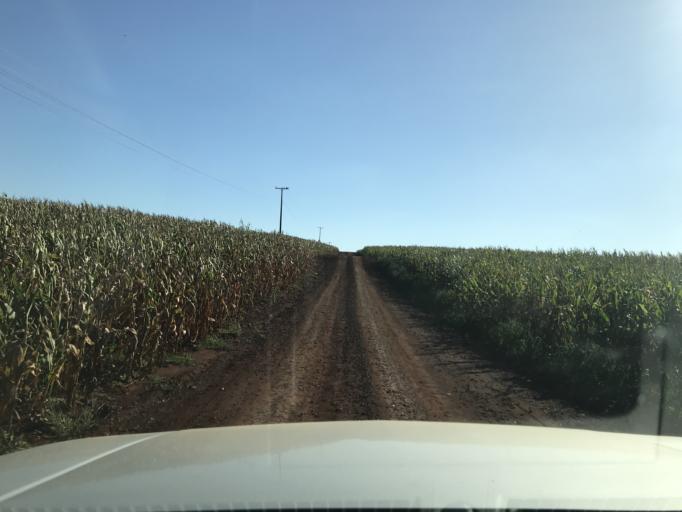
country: BR
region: Parana
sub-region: Palotina
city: Palotina
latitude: -24.2275
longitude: -53.8171
